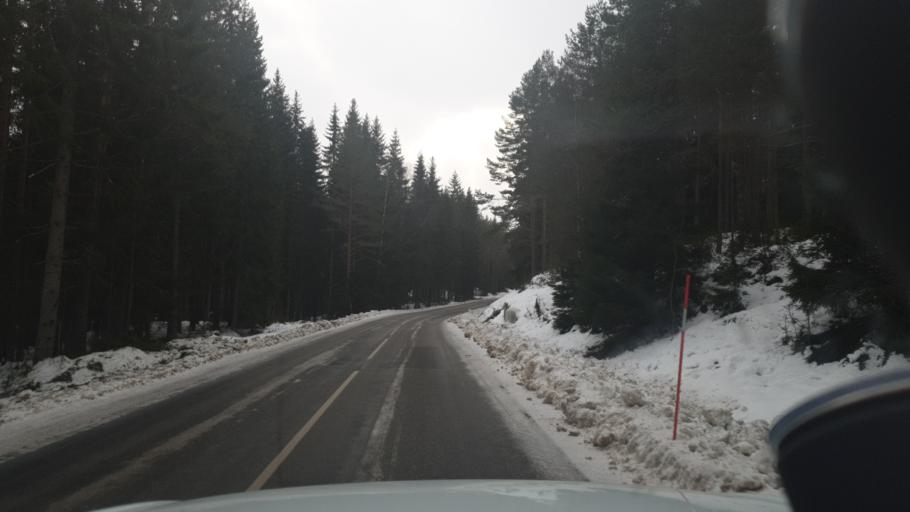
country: SE
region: Vaermland
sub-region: Eda Kommun
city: Amotfors
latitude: 59.5819
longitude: 12.2864
